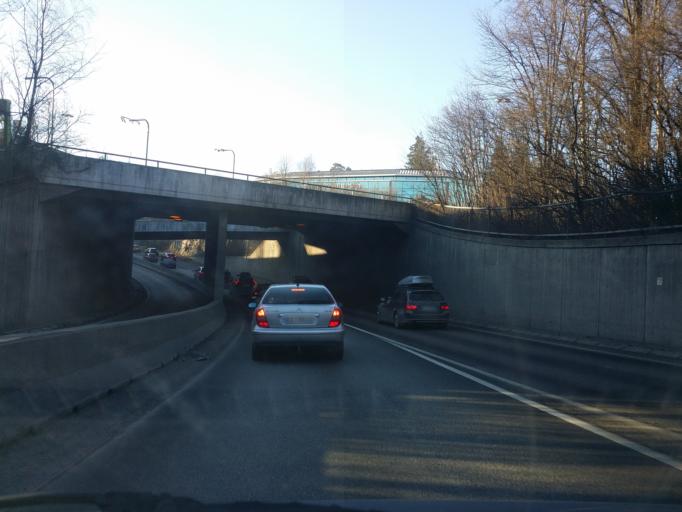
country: NO
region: Akershus
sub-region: Baerum
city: Lysaker
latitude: 59.9102
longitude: 10.6271
